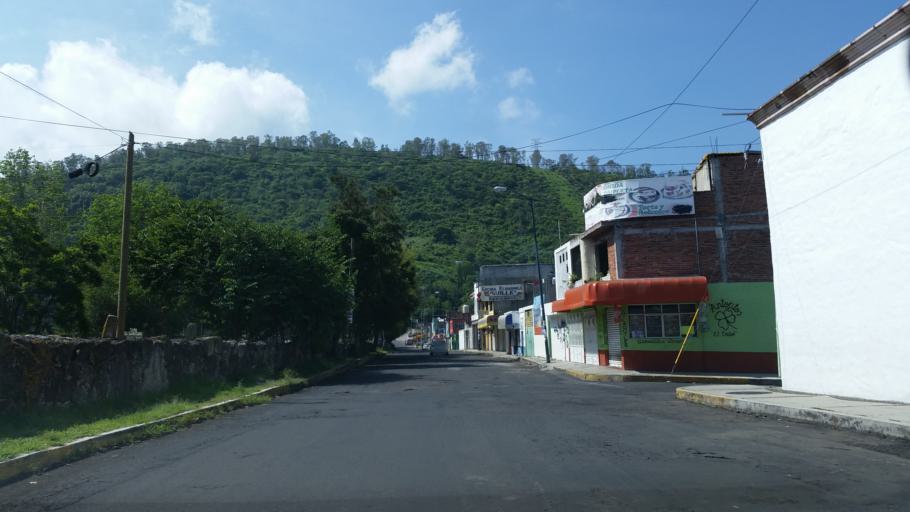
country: MX
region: Michoacan
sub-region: Morelia
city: Puerto de Buenavista (Lazaro Cardenas)
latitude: 19.6865
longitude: -101.1531
